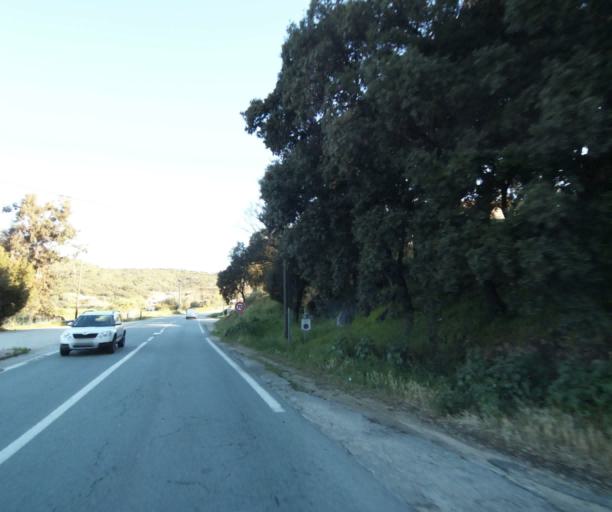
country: FR
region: Corsica
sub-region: Departement de la Corse-du-Sud
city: Propriano
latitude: 41.6585
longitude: 8.9175
